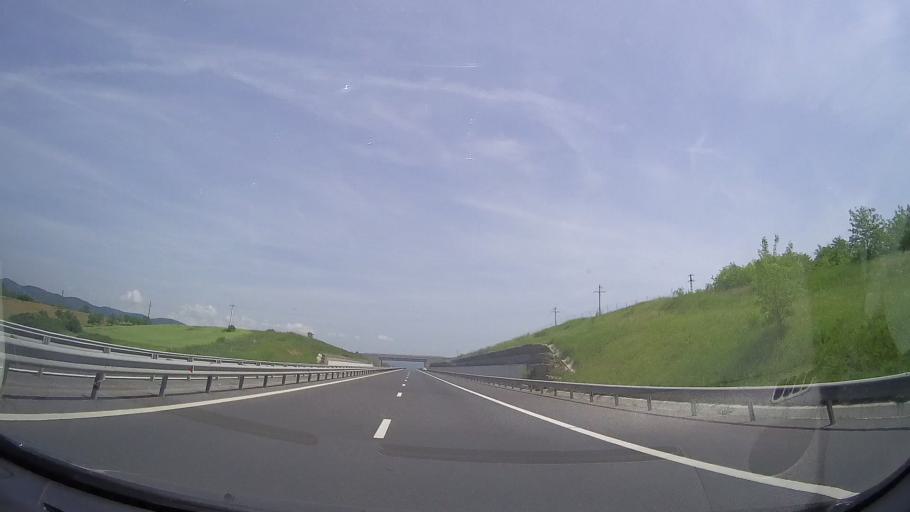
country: RO
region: Hunedoara
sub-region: Comuna Turdas
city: Turdas
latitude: 45.8444
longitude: 23.1283
